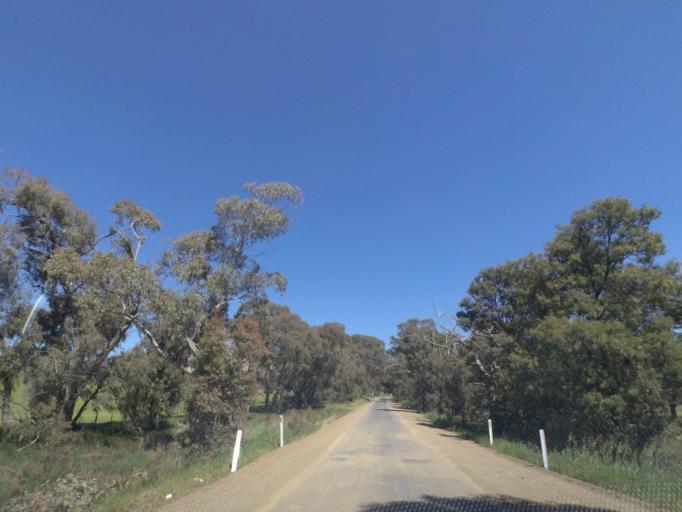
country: AU
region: Victoria
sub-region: Whittlesea
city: Whittlesea
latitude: -37.2898
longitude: 144.9905
